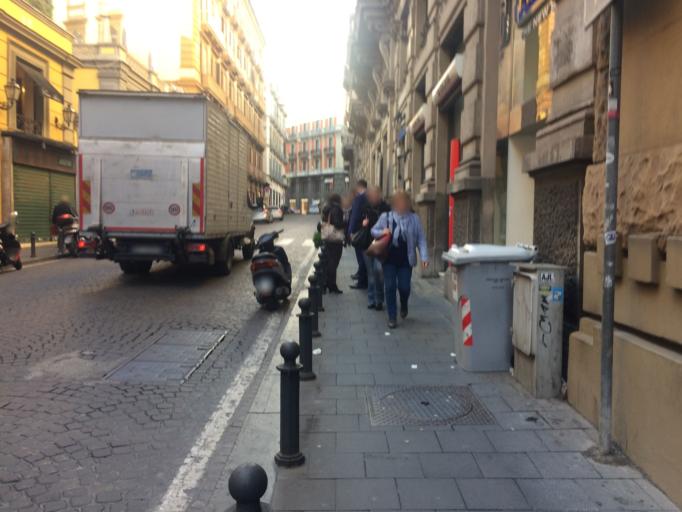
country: IT
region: Campania
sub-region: Provincia di Napoli
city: Napoli
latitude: 40.8358
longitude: 14.2412
